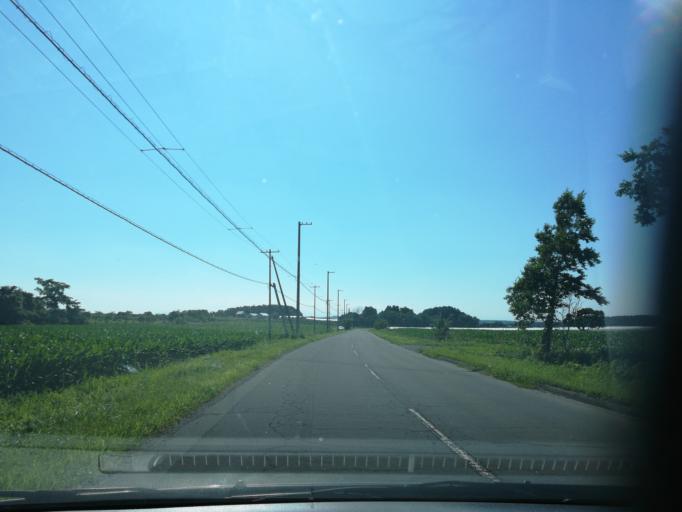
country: JP
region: Hokkaido
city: Chitose
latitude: 42.9160
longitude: 141.8421
